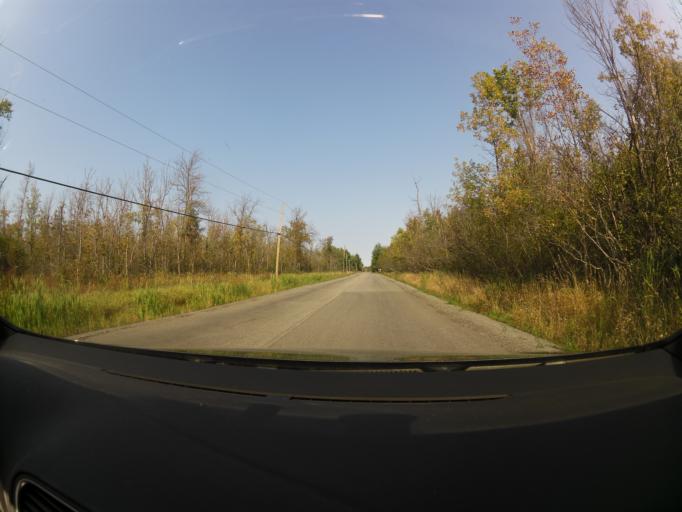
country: CA
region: Ontario
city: Carleton Place
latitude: 45.3087
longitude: -76.1233
